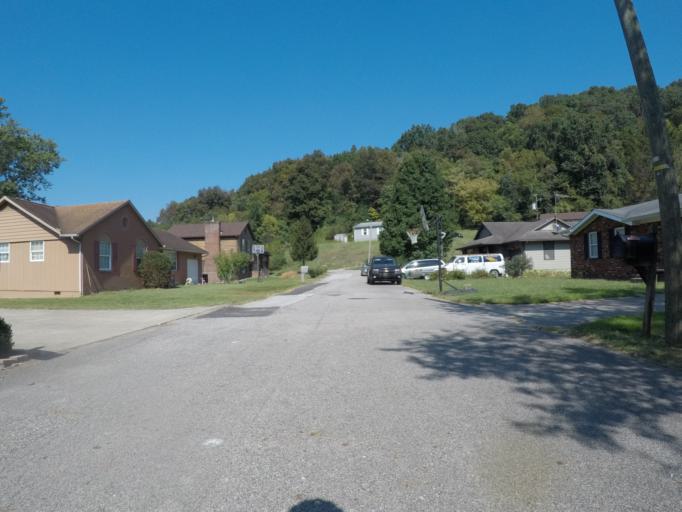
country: US
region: West Virginia
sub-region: Cabell County
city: Barboursville
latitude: 38.3703
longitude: -82.2714
